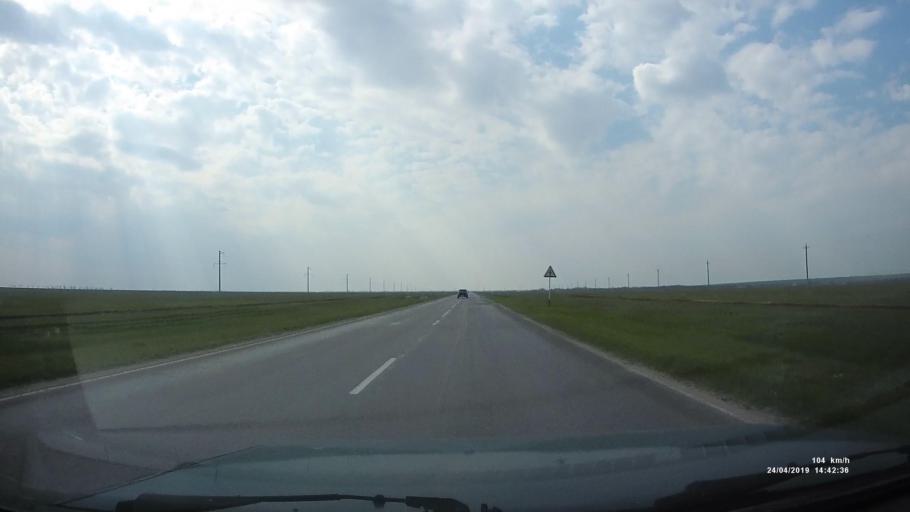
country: RU
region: Rostov
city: Remontnoye
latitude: 46.4529
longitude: 43.8585
